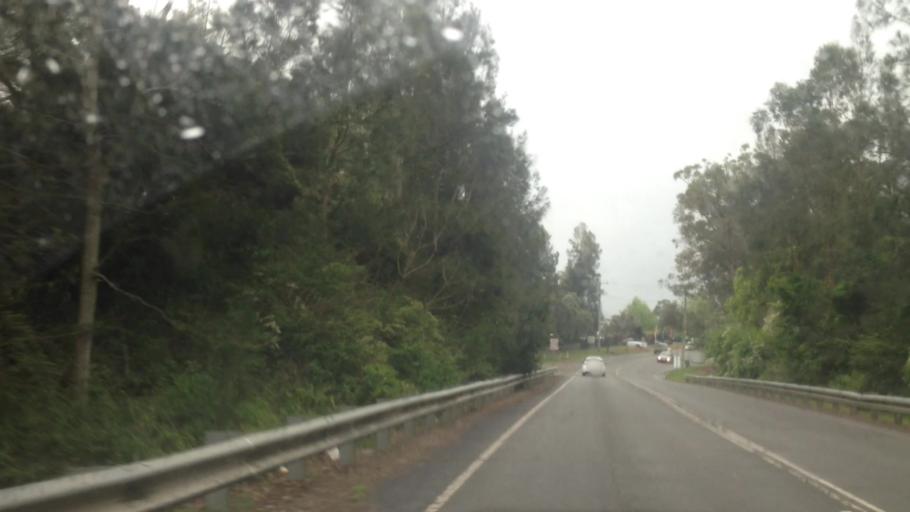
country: AU
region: New South Wales
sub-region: Lake Macquarie Shire
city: Dora Creek
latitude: -33.1002
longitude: 151.4744
